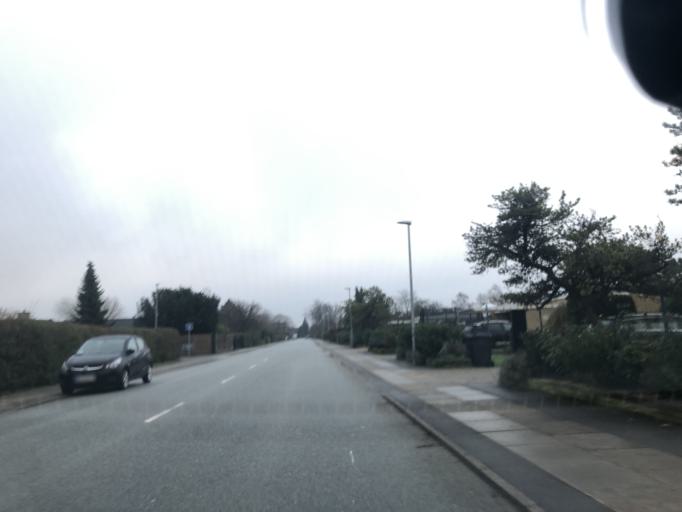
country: DK
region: Capital Region
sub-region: Tarnby Kommune
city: Tarnby
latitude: 55.6367
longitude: 12.5962
